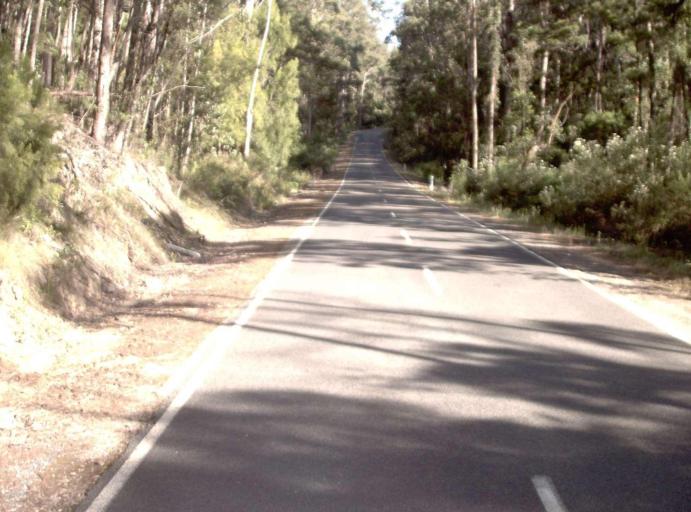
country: AU
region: Victoria
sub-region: East Gippsland
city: Lakes Entrance
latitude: -37.6456
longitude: 148.4817
